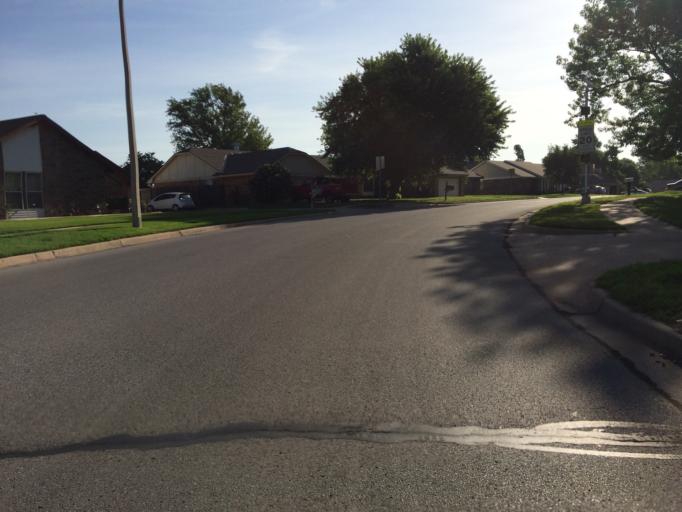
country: US
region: Oklahoma
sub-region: Cleveland County
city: Norman
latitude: 35.2239
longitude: -97.5037
